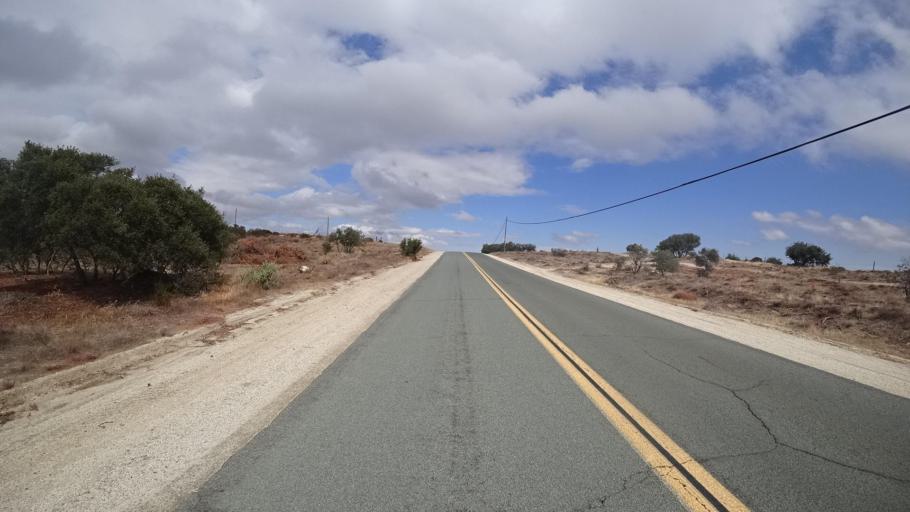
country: US
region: California
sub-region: San Diego County
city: Campo
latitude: 32.6568
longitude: -116.3151
